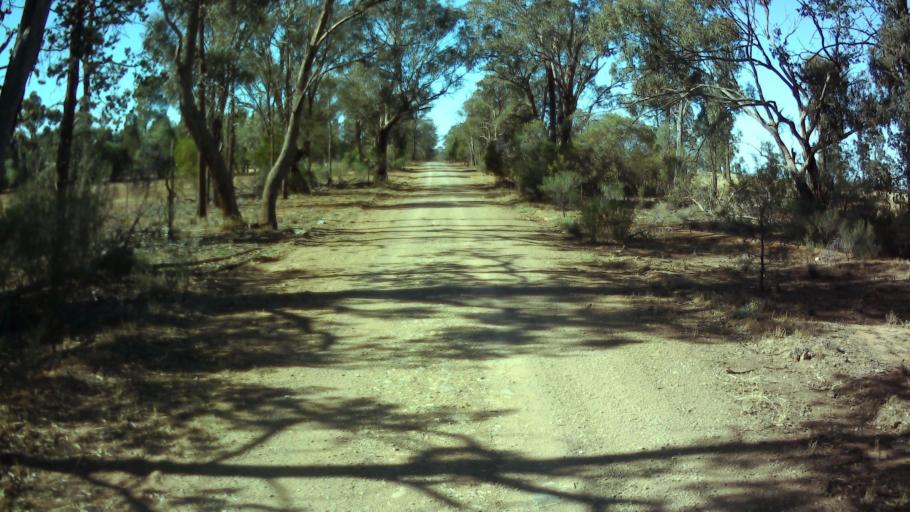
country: AU
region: New South Wales
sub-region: Weddin
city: Grenfell
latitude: -33.9247
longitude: 147.8741
